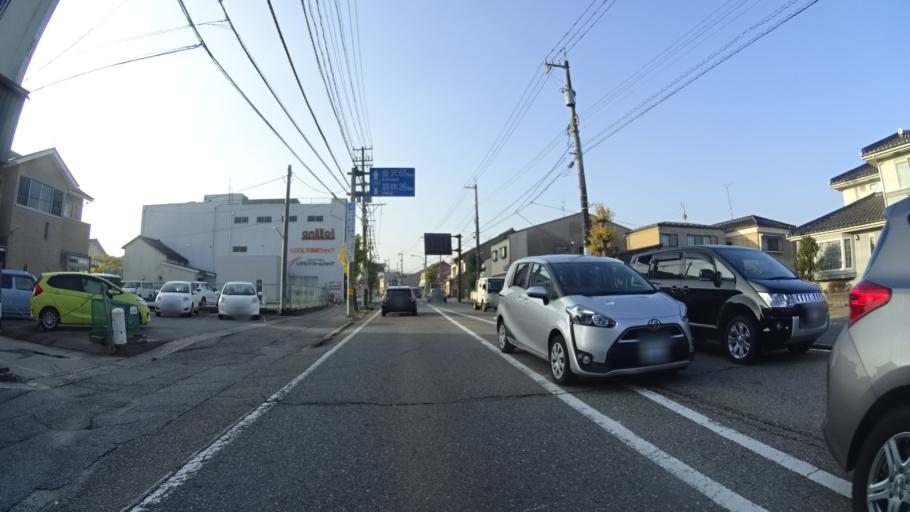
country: JP
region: Ishikawa
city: Nanao
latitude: 37.0415
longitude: 136.9697
